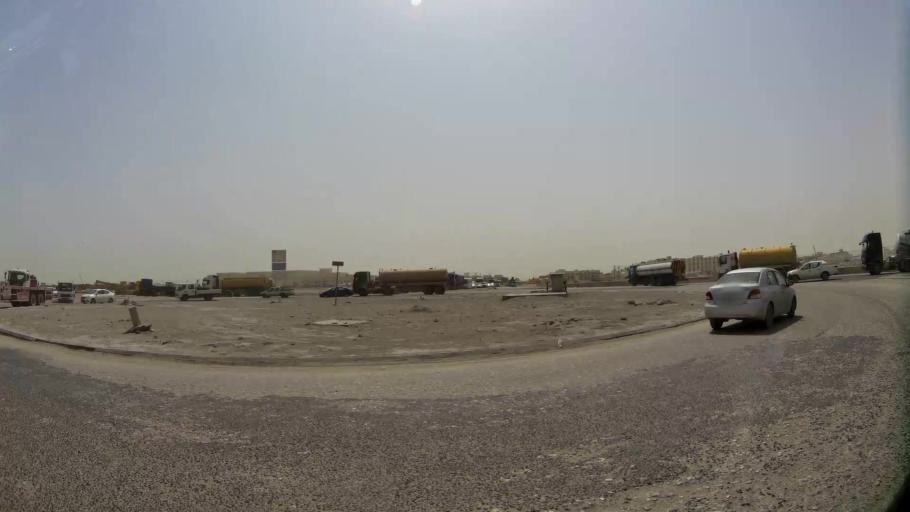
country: QA
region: Baladiyat ar Rayyan
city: Ar Rayyan
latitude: 25.1832
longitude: 51.4245
